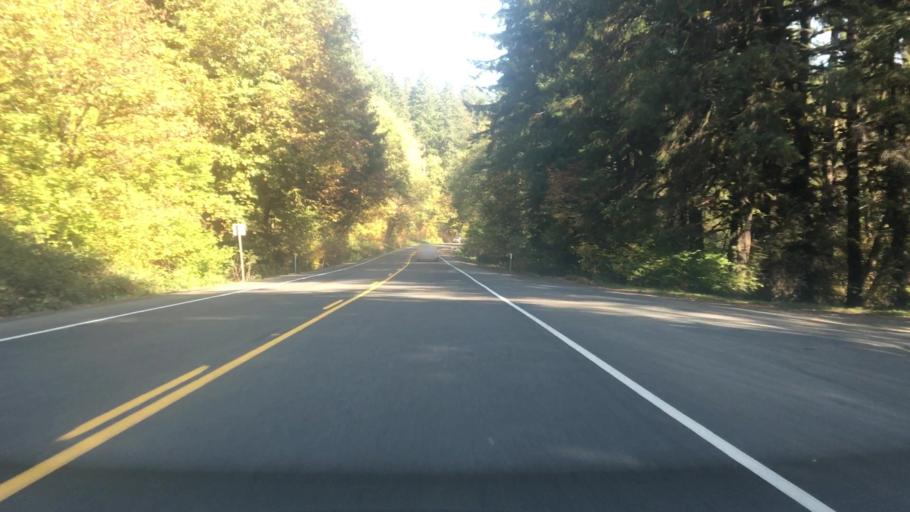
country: US
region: Oregon
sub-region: Lincoln County
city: Rose Lodge
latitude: 45.0513
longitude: -123.7799
